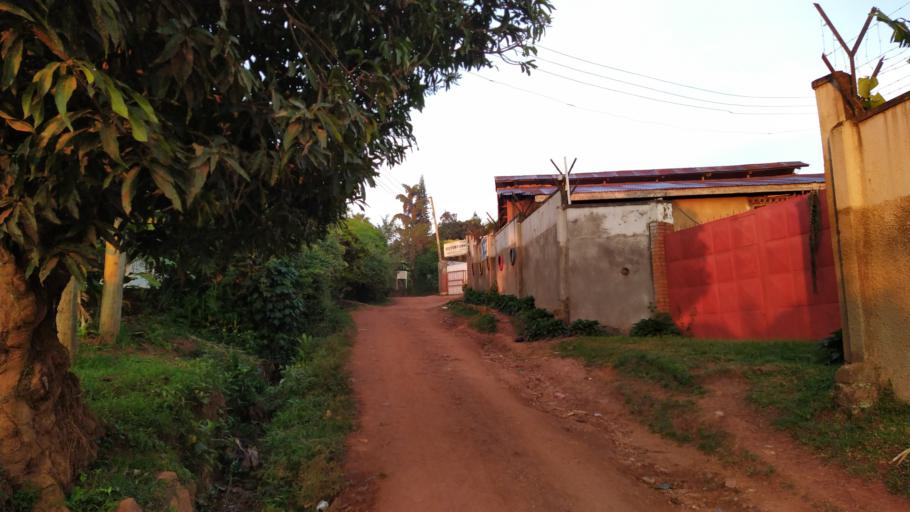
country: UG
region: Central Region
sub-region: Kampala District
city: Kampala
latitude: 0.2712
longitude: 32.5752
